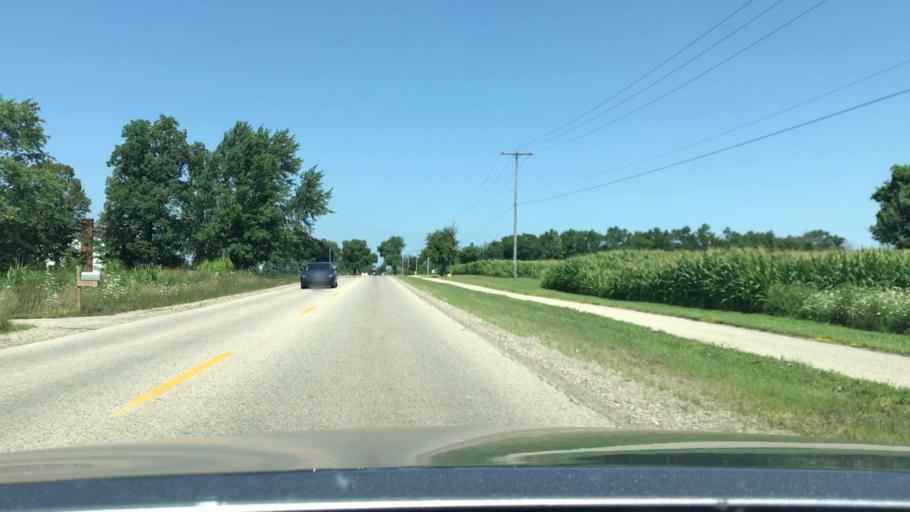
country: US
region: Michigan
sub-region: Ottawa County
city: Holland
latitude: 42.8443
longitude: -86.0790
